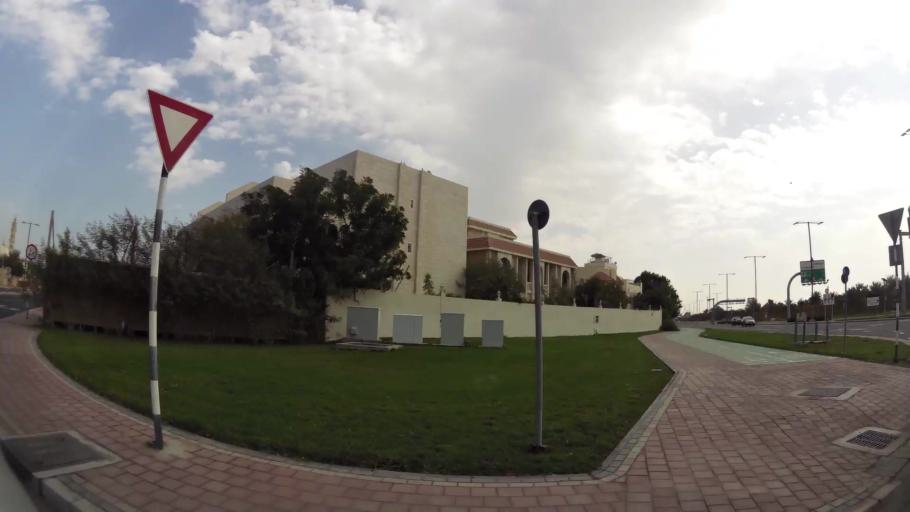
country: AE
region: Abu Dhabi
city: Abu Dhabi
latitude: 24.4552
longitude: 54.3474
